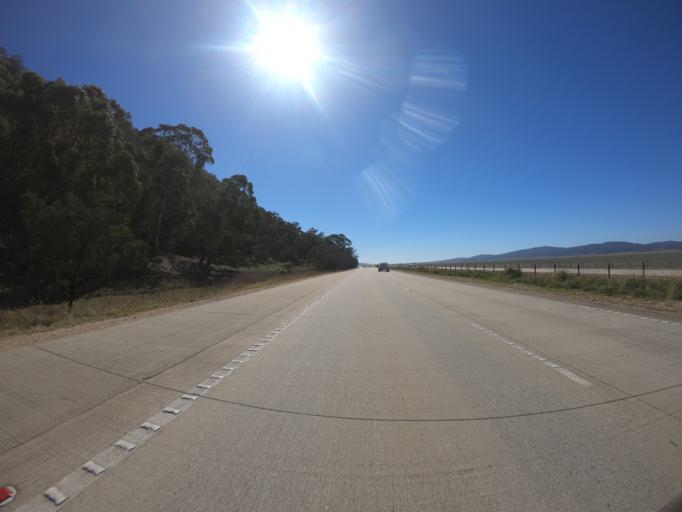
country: AU
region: New South Wales
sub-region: Yass Valley
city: Gundaroo
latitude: -35.0473
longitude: 149.3761
